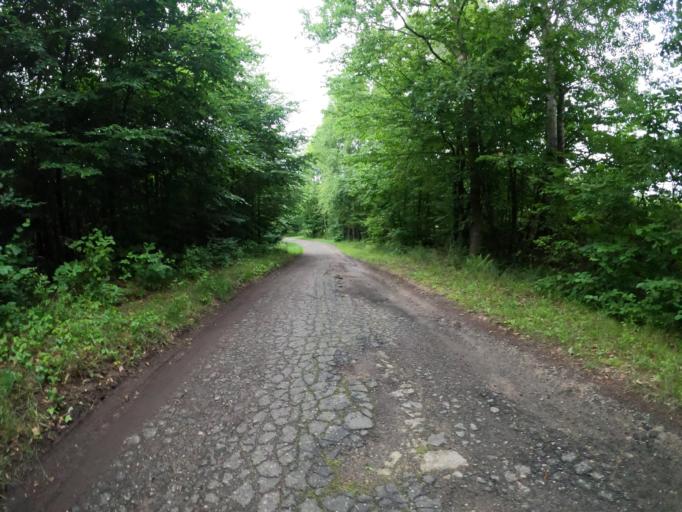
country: PL
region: West Pomeranian Voivodeship
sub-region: Powiat szczecinecki
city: Grzmiaca
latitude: 53.9610
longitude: 16.4554
